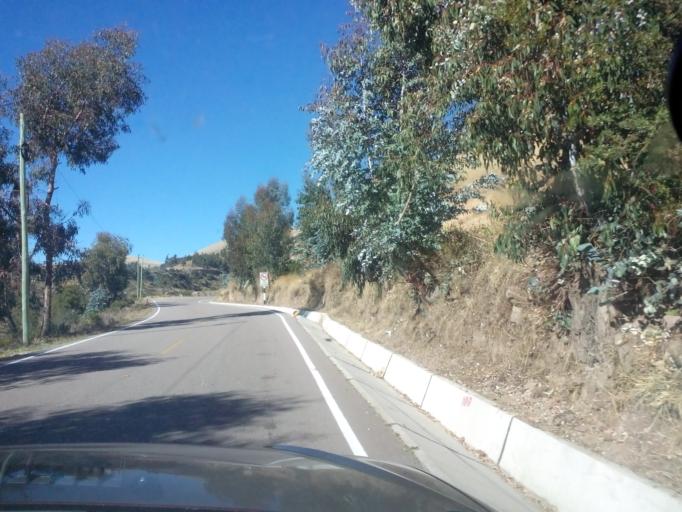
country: PE
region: Ayacucho
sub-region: Provincia de Huamanga
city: Chiara
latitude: -13.2841
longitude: -74.2305
